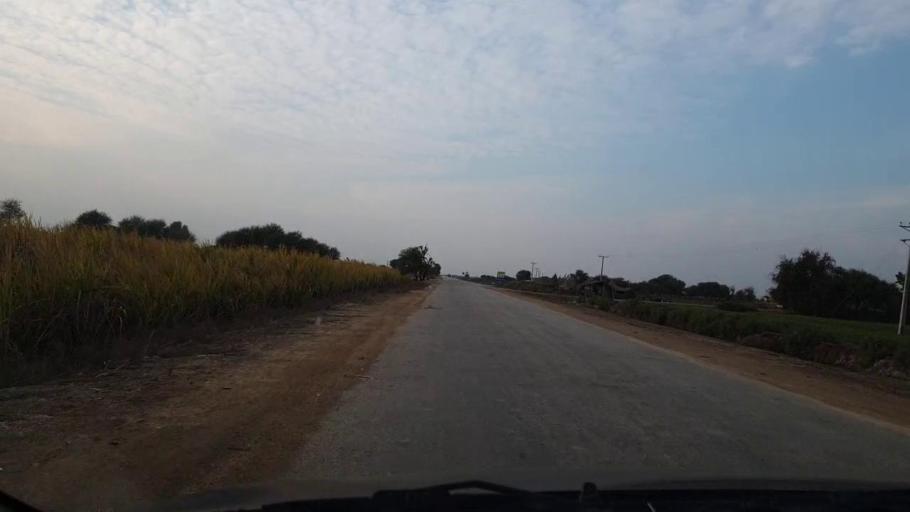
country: PK
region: Sindh
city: Jhol
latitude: 25.9902
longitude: 68.8570
